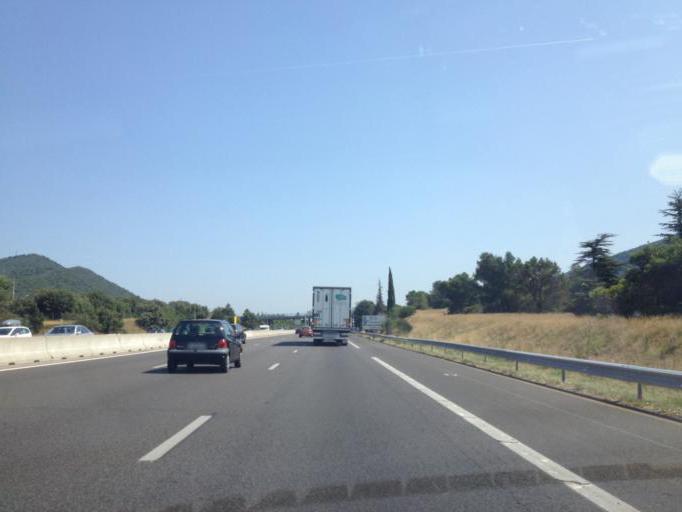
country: FR
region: Rhone-Alpes
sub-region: Departement de la Drome
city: Malataverne
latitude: 44.4591
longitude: 4.7586
